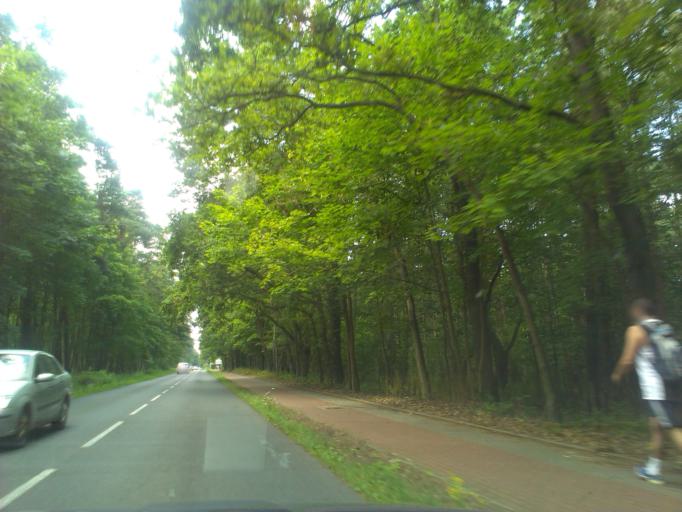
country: PL
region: West Pomeranian Voivodeship
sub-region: Powiat kamienski
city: Dziwnow
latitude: 54.0011
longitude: 14.6806
